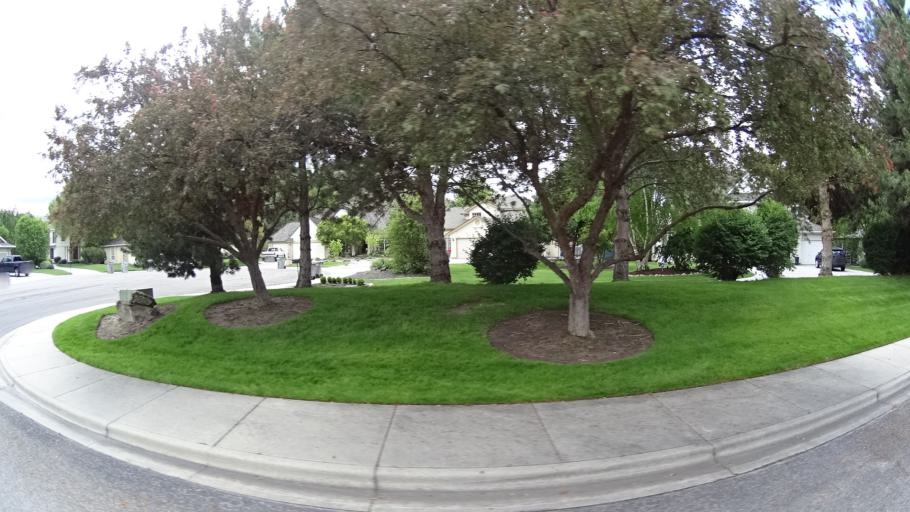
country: US
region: Idaho
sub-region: Ada County
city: Garden City
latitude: 43.6652
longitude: -116.2174
